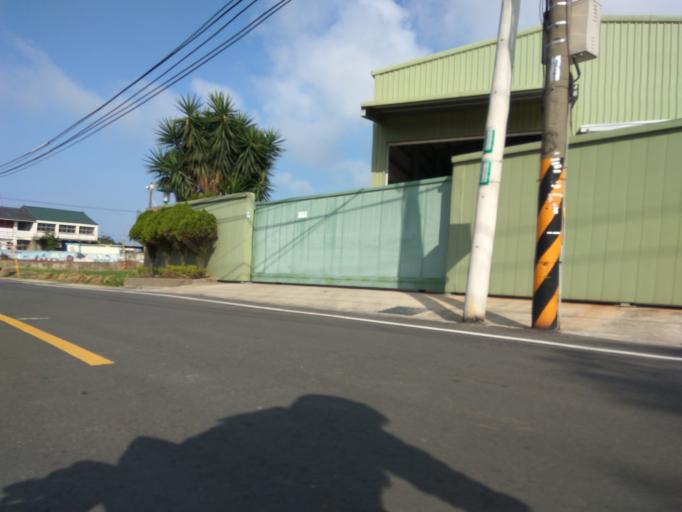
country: TW
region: Taiwan
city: Taoyuan City
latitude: 25.0642
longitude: 121.1727
